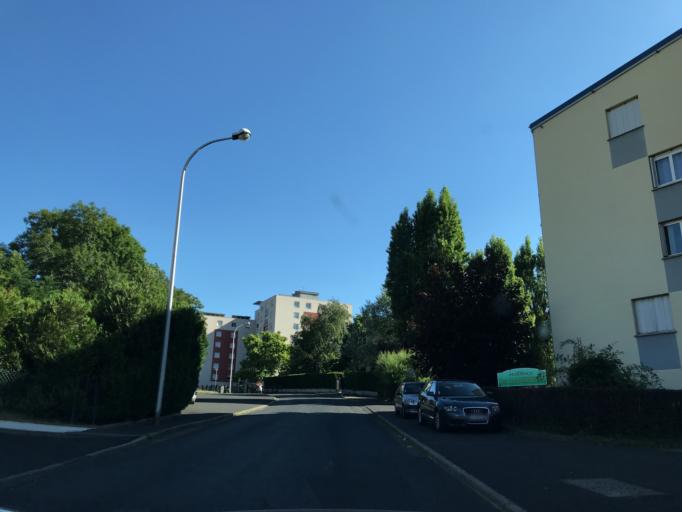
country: FR
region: Auvergne
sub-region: Departement du Puy-de-Dome
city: Thiers
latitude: 45.8474
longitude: 3.5331
